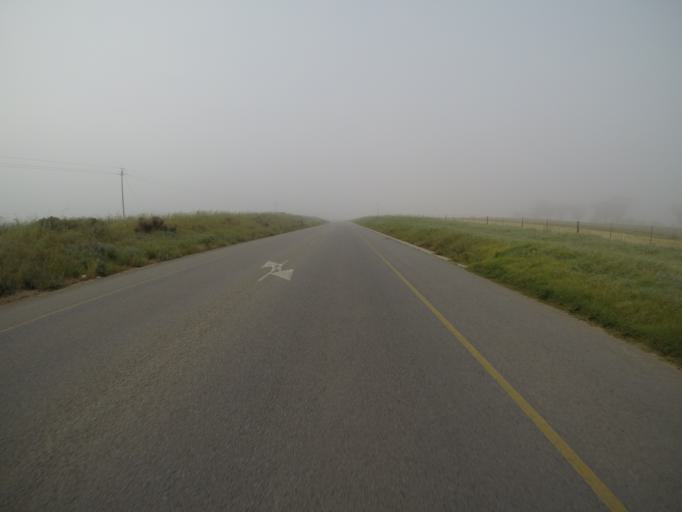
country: ZA
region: Western Cape
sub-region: City of Cape Town
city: Kraaifontein
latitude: -33.6896
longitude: 18.7042
